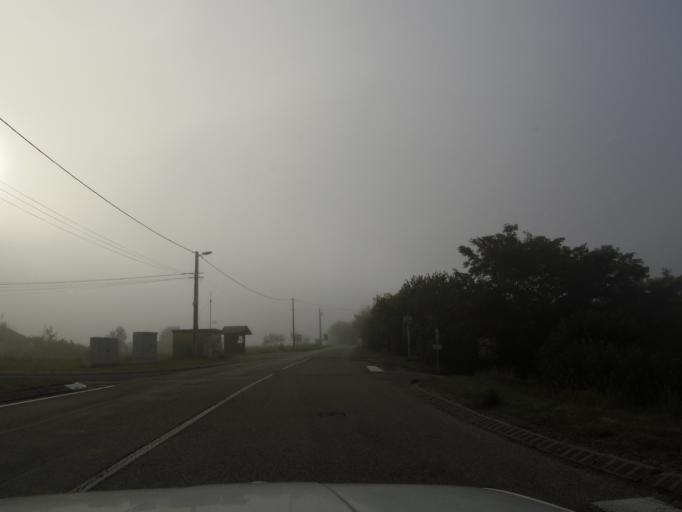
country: FR
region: Rhone-Alpes
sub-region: Departement de l'Isere
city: Creys-Mepieu
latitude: 45.7788
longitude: 5.4708
